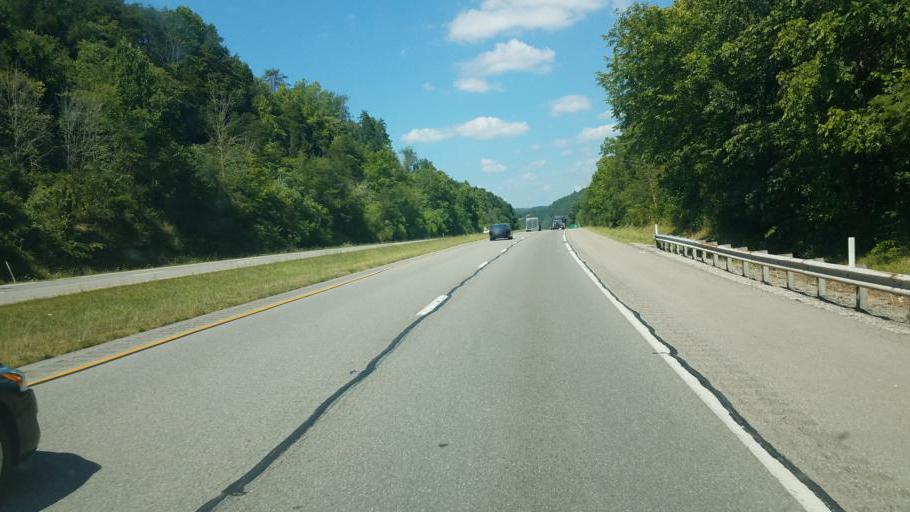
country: US
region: West Virginia
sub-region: Kanawha County
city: Sissonville
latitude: 38.5371
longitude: -81.6437
